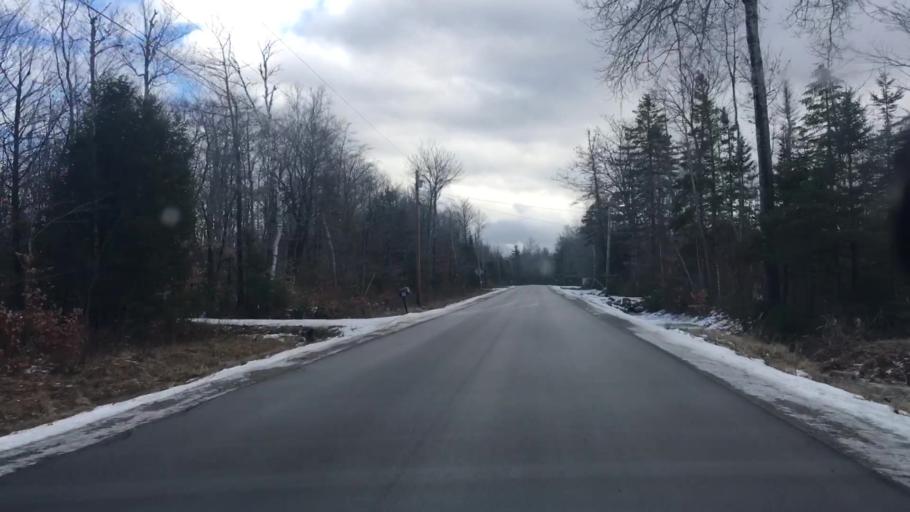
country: US
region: Maine
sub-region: Hancock County
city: Dedham
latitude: 44.6823
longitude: -68.7080
